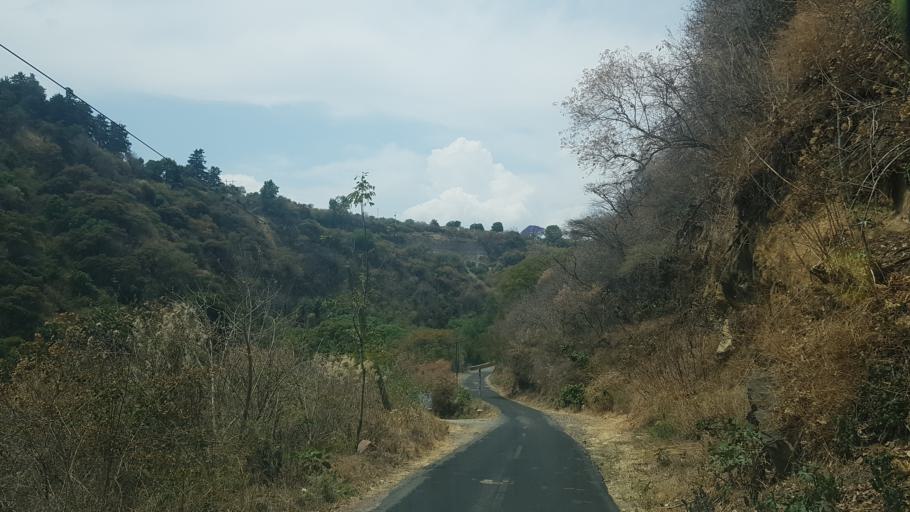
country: MX
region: Puebla
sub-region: Tochimilco
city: La Magdalena Yancuitlalpan
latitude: 18.8728
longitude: -98.6055
